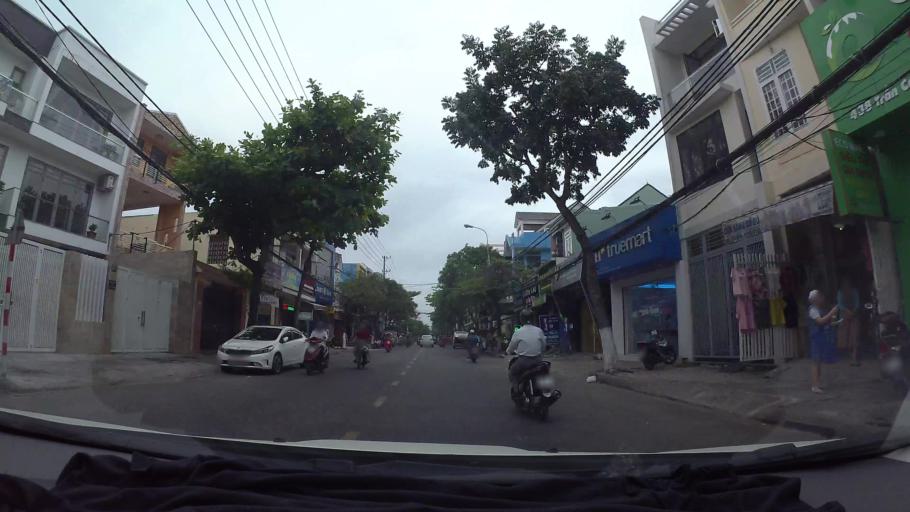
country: VN
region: Da Nang
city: Thanh Khe
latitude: 16.0711
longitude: 108.1977
